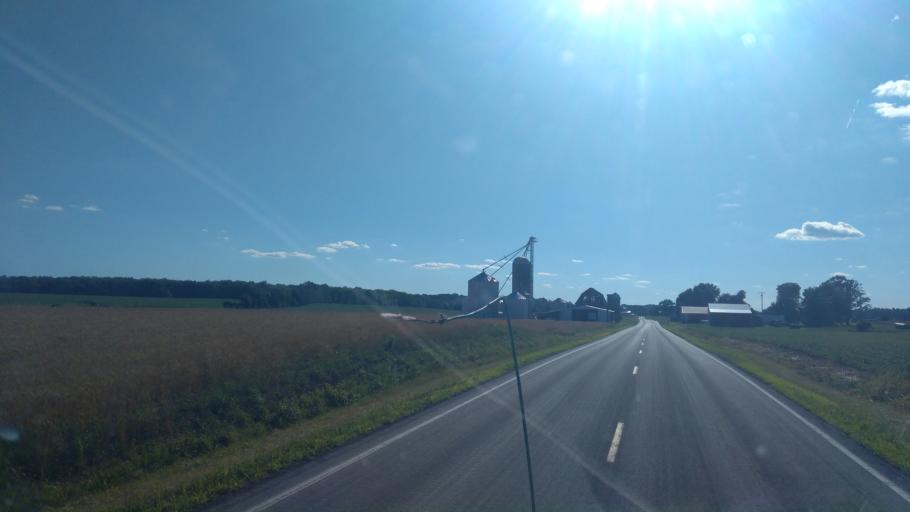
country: US
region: New York
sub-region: Wayne County
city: Clyde
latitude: 43.0009
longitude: -76.8809
